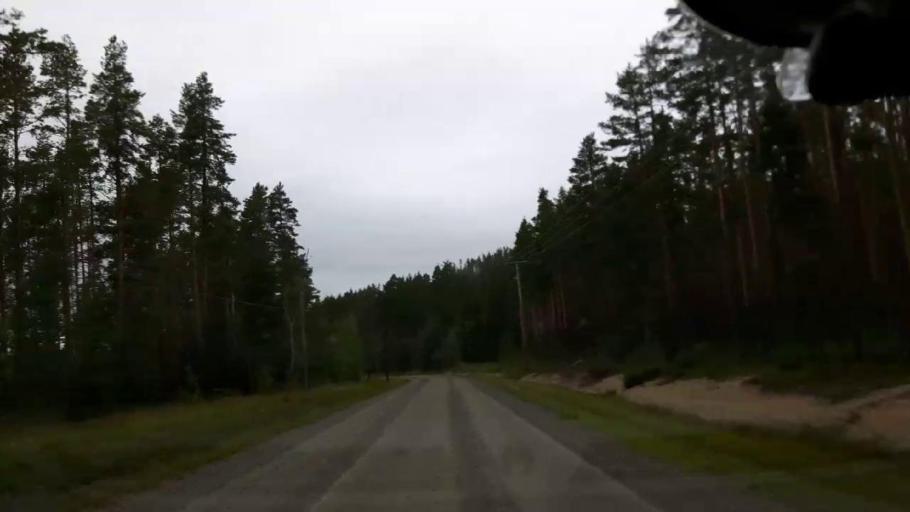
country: SE
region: Vaesternorrland
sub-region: Ange Kommun
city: Fransta
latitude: 62.7862
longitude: 16.0638
